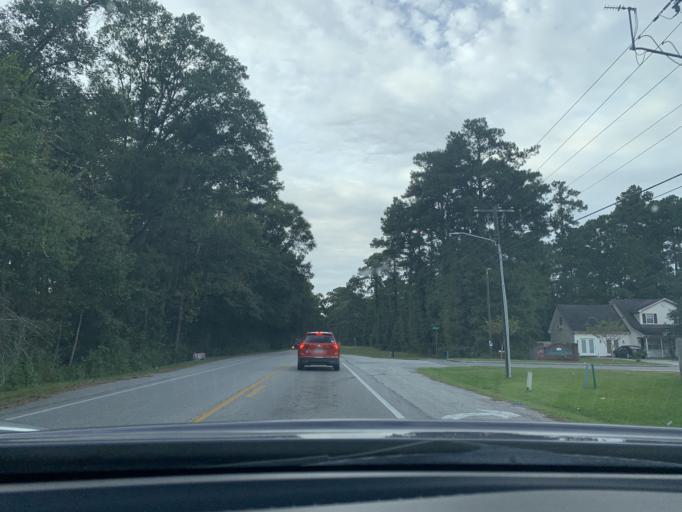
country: US
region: Georgia
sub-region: Chatham County
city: Georgetown
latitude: 32.0355
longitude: -81.2555
